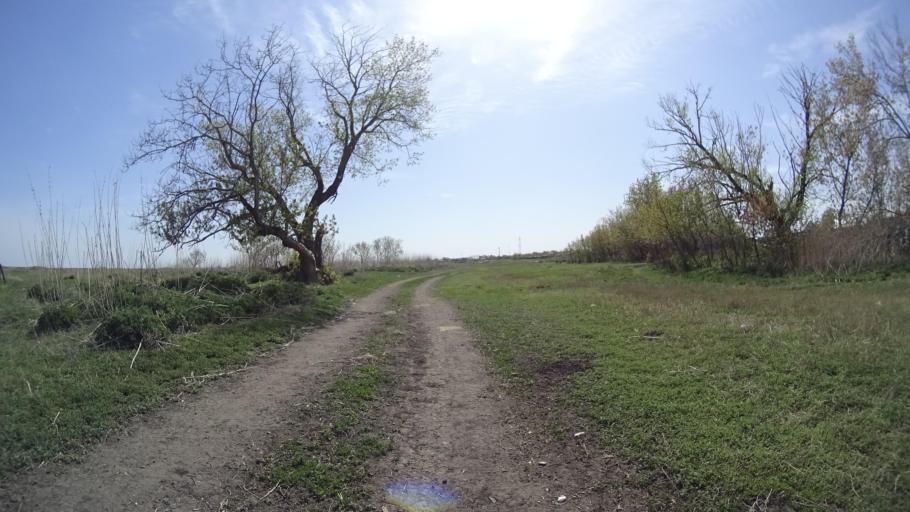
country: RU
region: Chelyabinsk
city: Chesma
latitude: 53.8020
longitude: 61.0208
